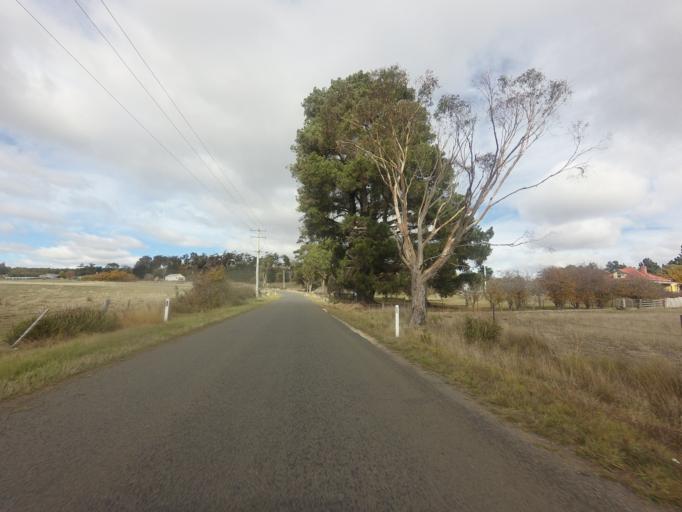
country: AU
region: Tasmania
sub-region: Brighton
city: Bridgewater
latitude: -42.4091
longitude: 147.3980
